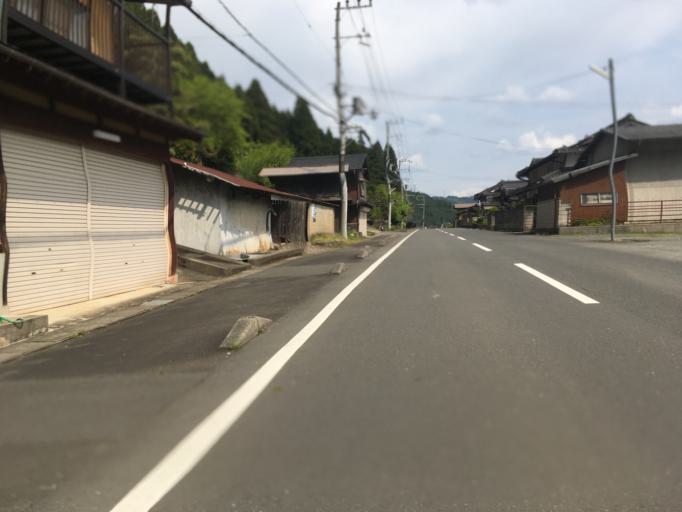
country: JP
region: Kyoto
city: Kameoka
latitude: 35.1449
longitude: 135.5809
